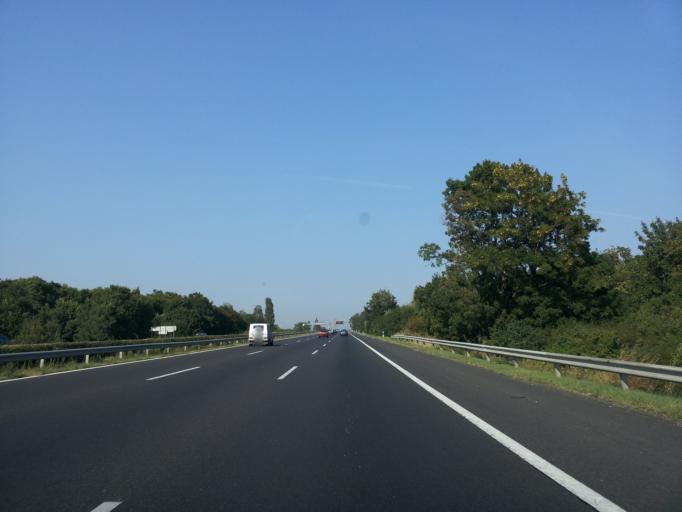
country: HU
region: Fejer
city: Martonvasar
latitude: 47.3406
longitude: 18.7883
